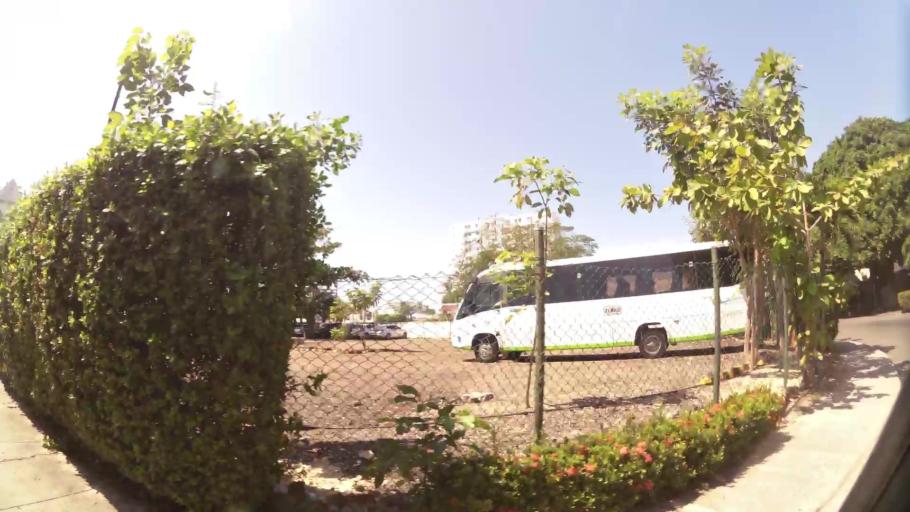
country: CO
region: Bolivar
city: Cartagena
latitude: 10.4473
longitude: -75.5167
